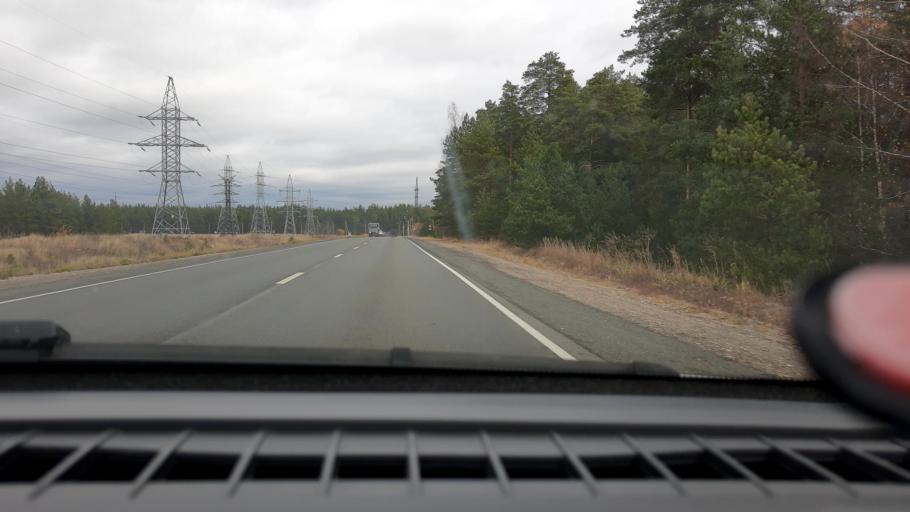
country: RU
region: Nizjnij Novgorod
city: Lukino
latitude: 56.3991
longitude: 43.6514
